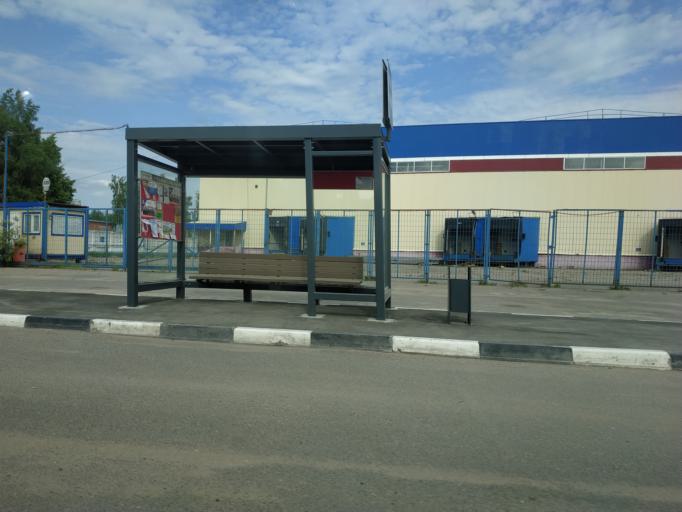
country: RU
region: Moskovskaya
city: Ramenskoye
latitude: 55.5633
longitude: 38.2636
